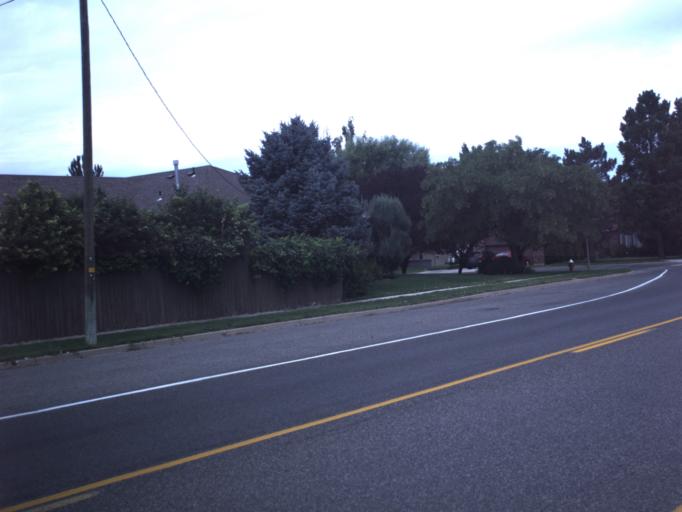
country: US
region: Utah
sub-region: Weber County
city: West Haven
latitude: 41.1720
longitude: -112.0644
